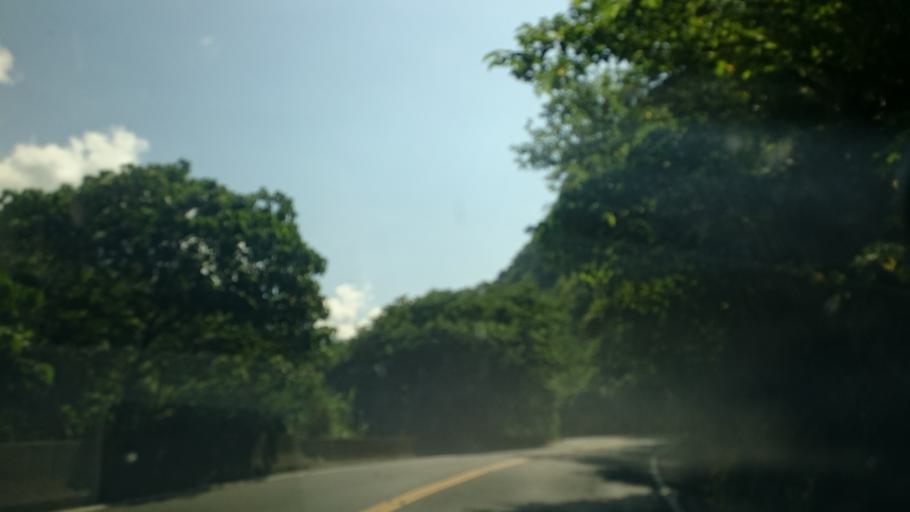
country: TW
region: Taiwan
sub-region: Nantou
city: Puli
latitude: 23.9930
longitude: 121.0296
